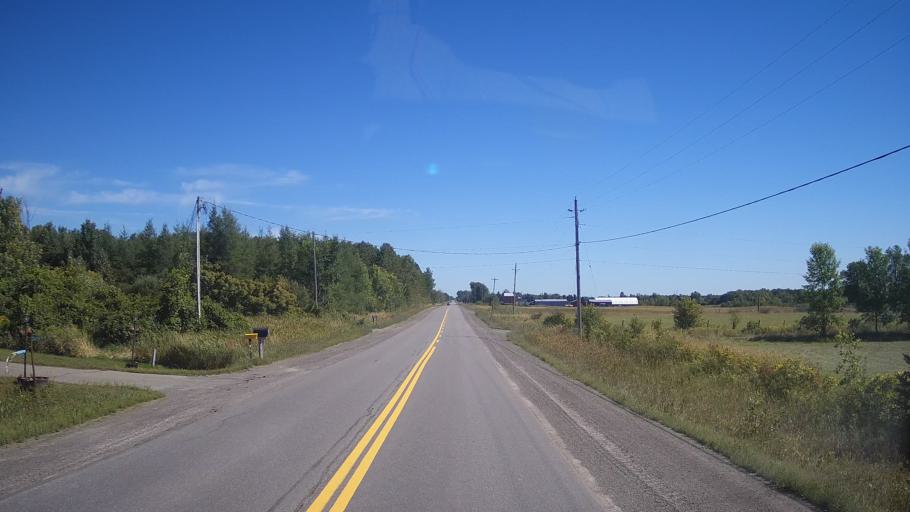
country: CA
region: Ontario
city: Bells Corners
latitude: 45.0271
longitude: -75.7270
